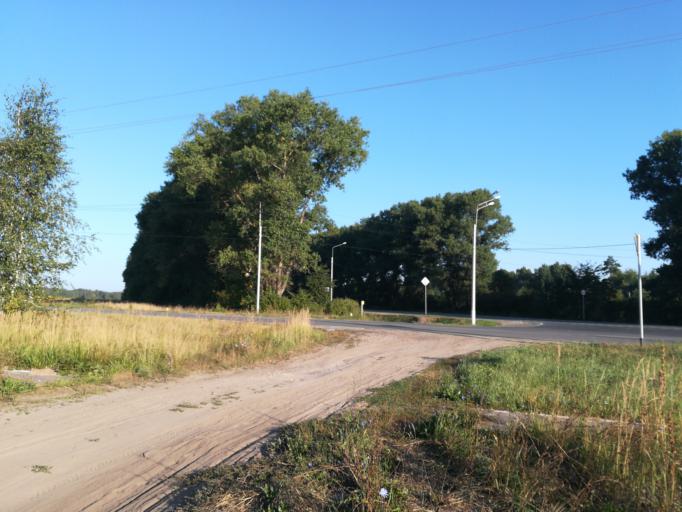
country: RU
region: Brjansk
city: Karachev
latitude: 53.1288
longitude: 34.9336
